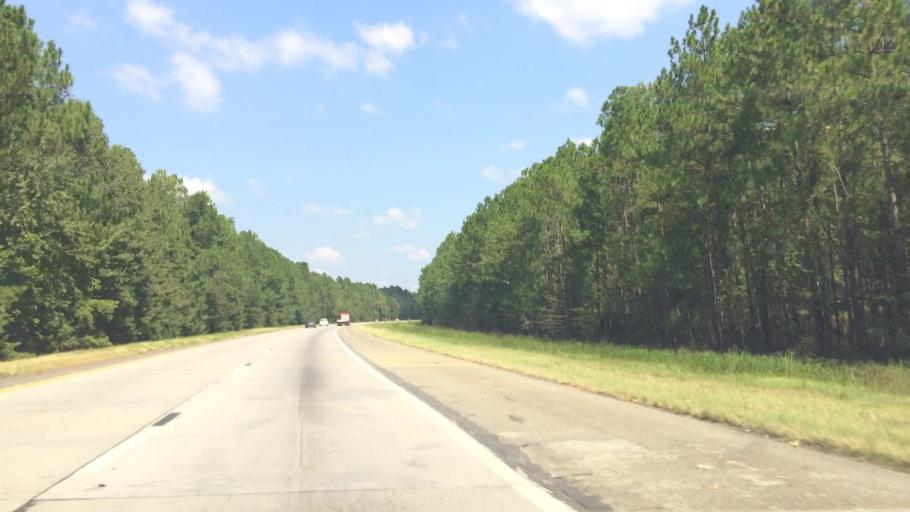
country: US
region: South Carolina
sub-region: Colleton County
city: Walterboro
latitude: 33.0451
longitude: -80.6690
